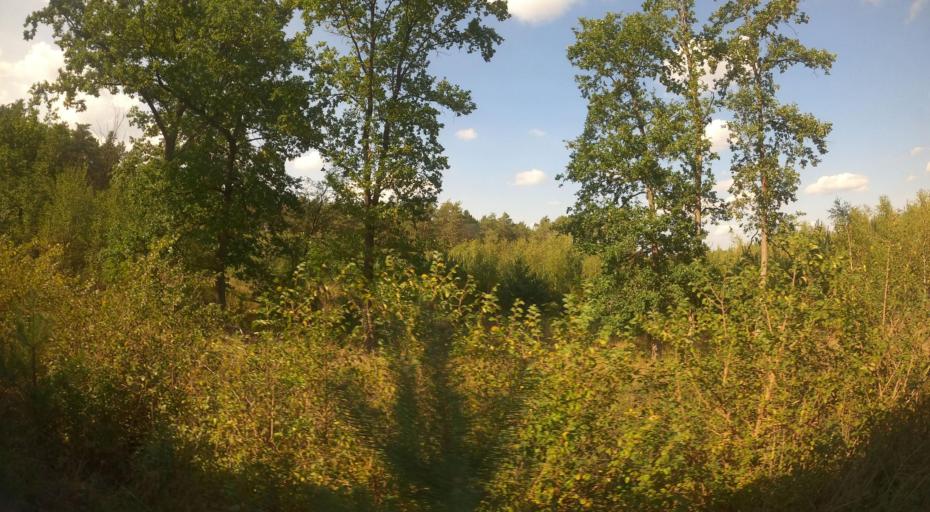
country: PL
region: Lubusz
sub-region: Powiat zielonogorski
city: Swidnica
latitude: 51.9232
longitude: 15.3755
